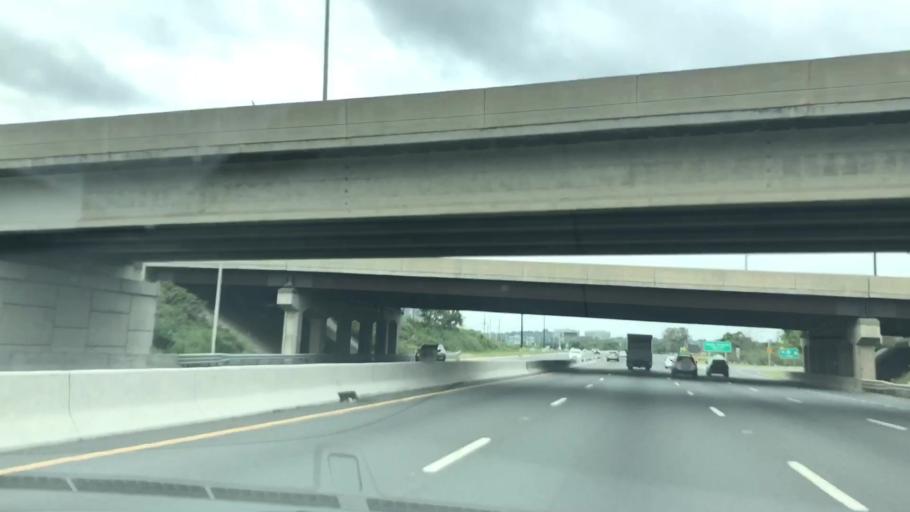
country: US
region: New Jersey
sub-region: Hudson County
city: Secaucus
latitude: 40.8084
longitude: -74.0788
